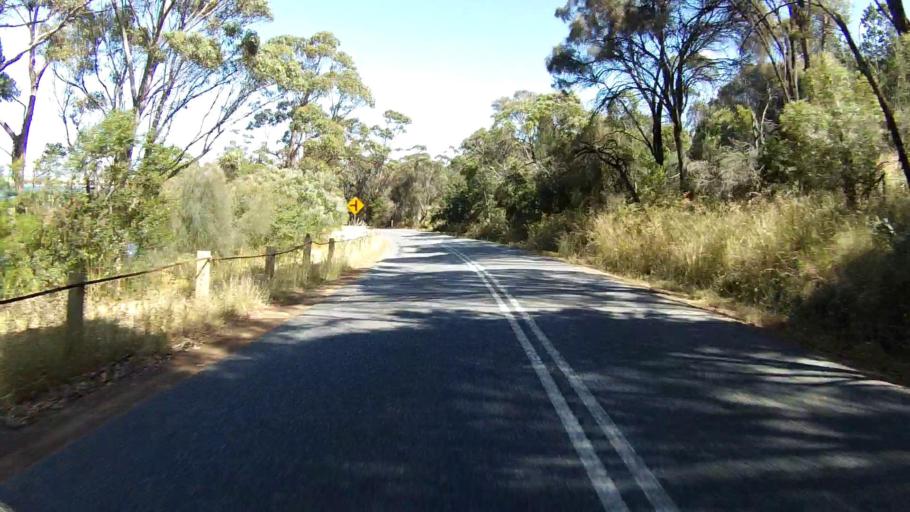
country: AU
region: Tasmania
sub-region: Sorell
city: Sorell
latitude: -42.2388
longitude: 148.0125
